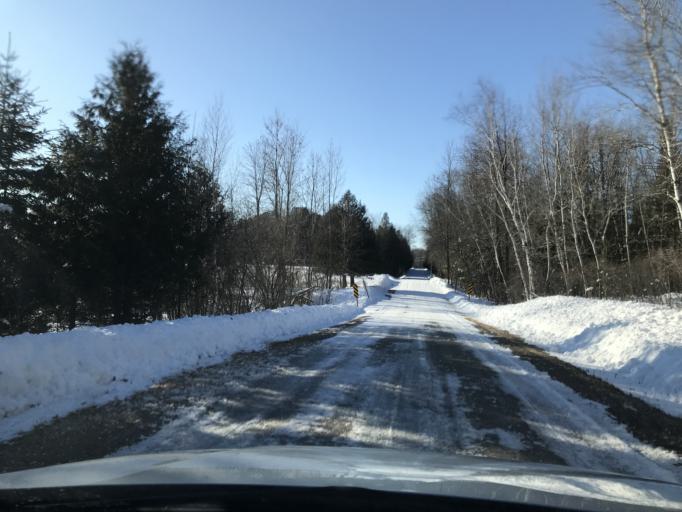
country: US
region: Wisconsin
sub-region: Oconto County
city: Oconto
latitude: 44.9544
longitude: -87.9770
